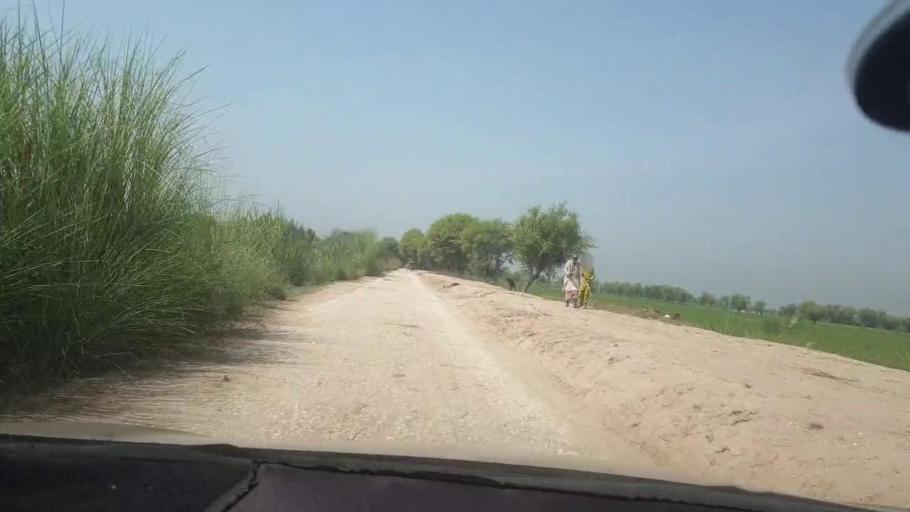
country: PK
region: Sindh
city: Shahdadkot
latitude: 27.7191
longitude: 67.9458
